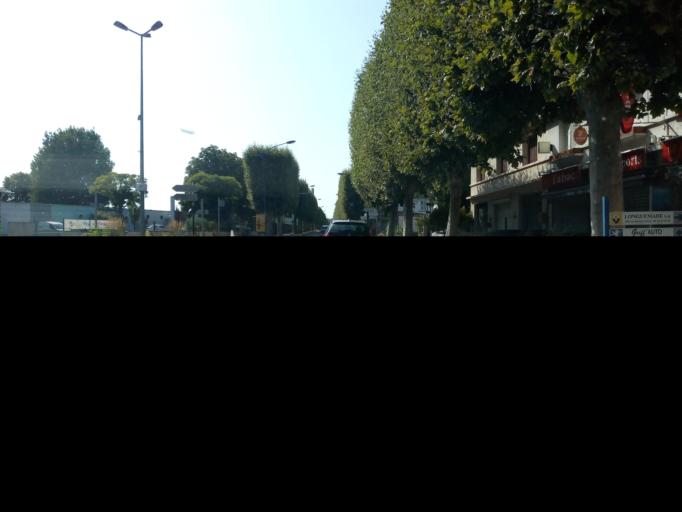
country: FR
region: Haute-Normandie
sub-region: Departement de la Seine-Maritime
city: Sotteville-les-Rouen
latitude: 49.4067
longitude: 1.0962
